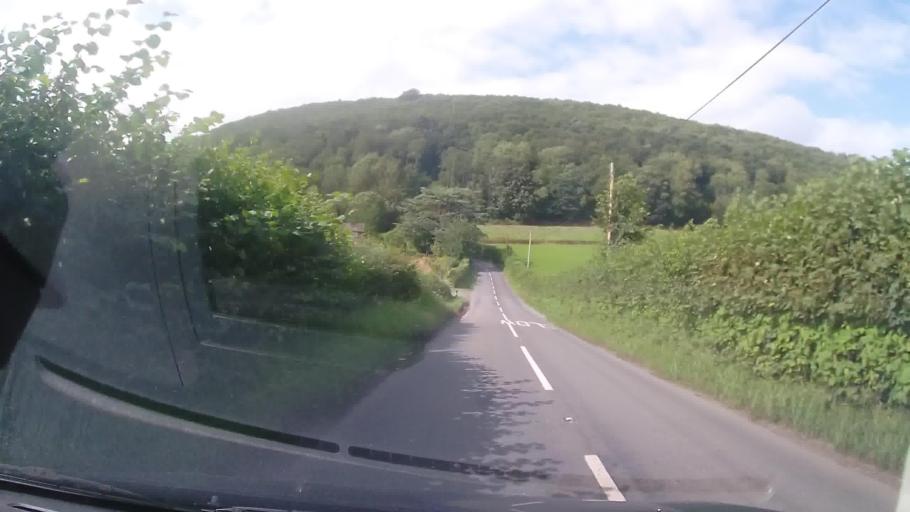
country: GB
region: Wales
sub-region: Sir Powys
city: Knighton
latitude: 52.3503
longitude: -3.0273
